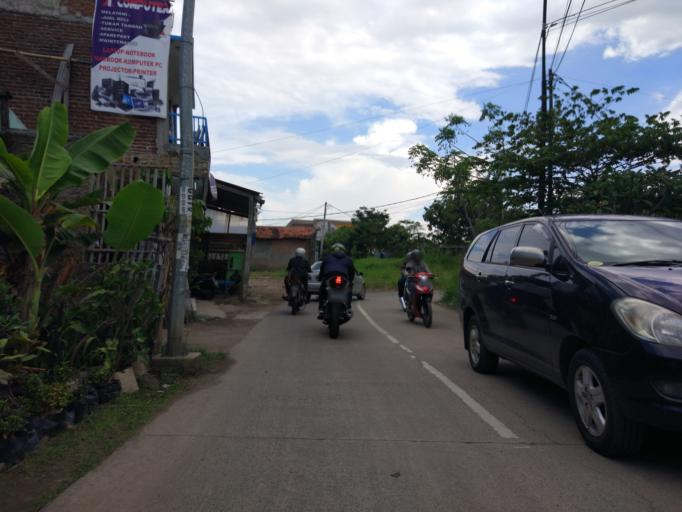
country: ID
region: West Java
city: Bandung
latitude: -6.9226
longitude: 107.6694
